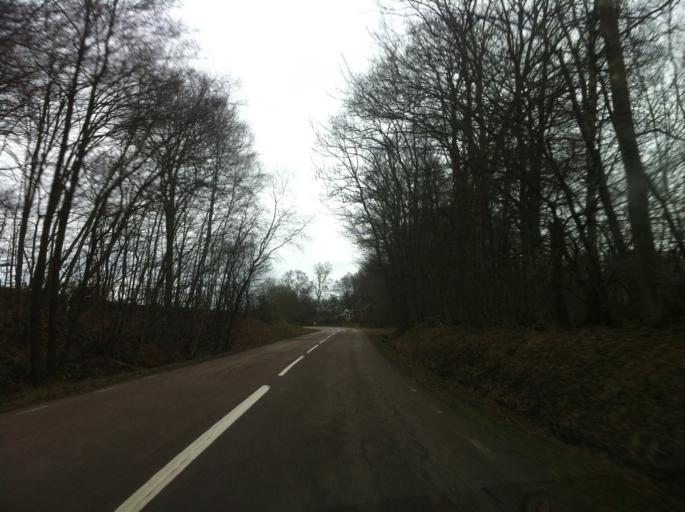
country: SE
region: Skane
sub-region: Svalovs Kommun
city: Kagerod
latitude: 56.0361
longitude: 13.0995
